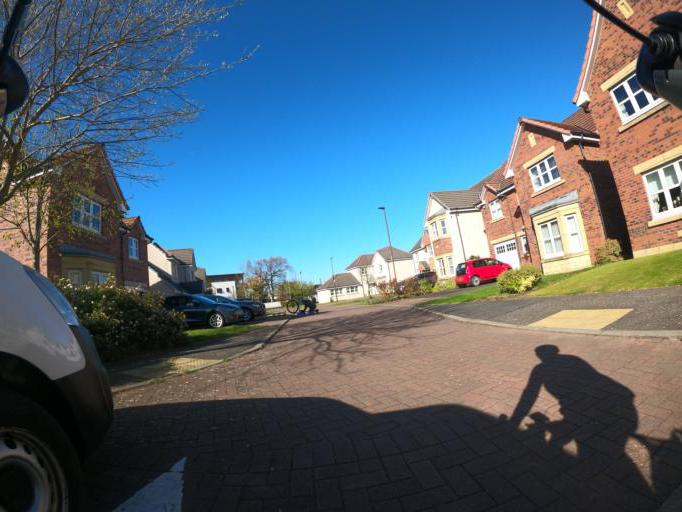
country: GB
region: Scotland
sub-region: Edinburgh
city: Currie
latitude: 55.9457
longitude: -3.3085
